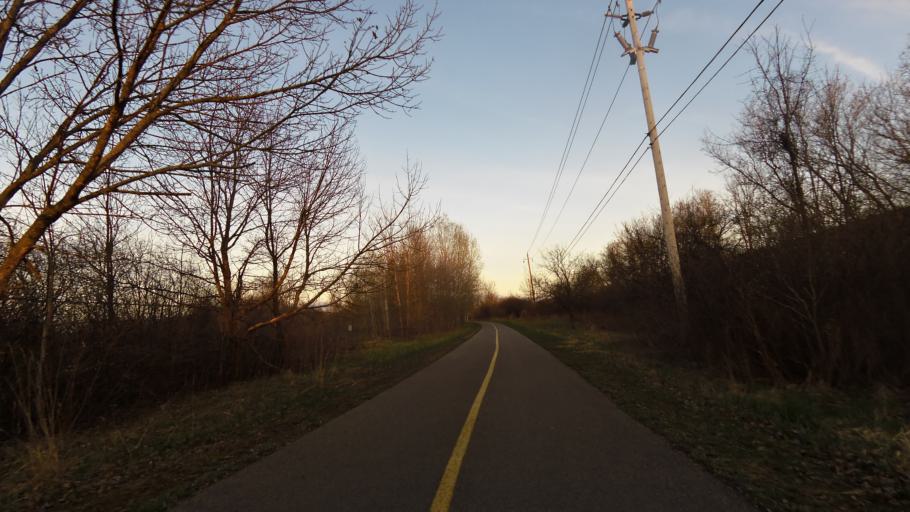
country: CA
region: Ontario
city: Bells Corners
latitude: 45.3432
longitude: -75.8779
